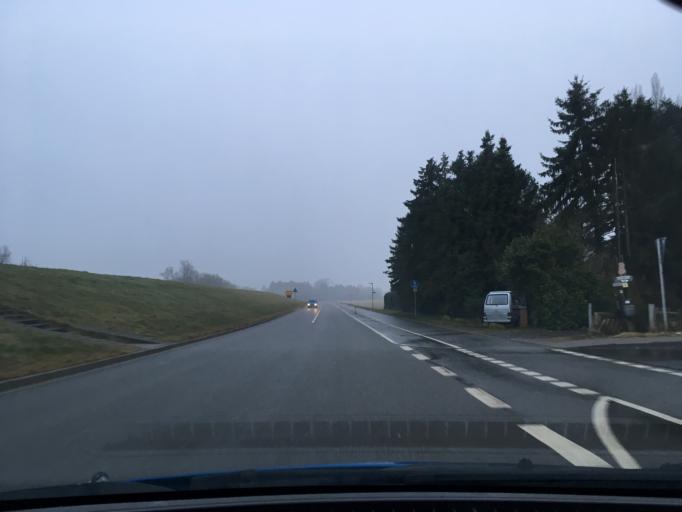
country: DE
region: Lower Saxony
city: Stelle
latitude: 53.4289
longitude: 10.1000
